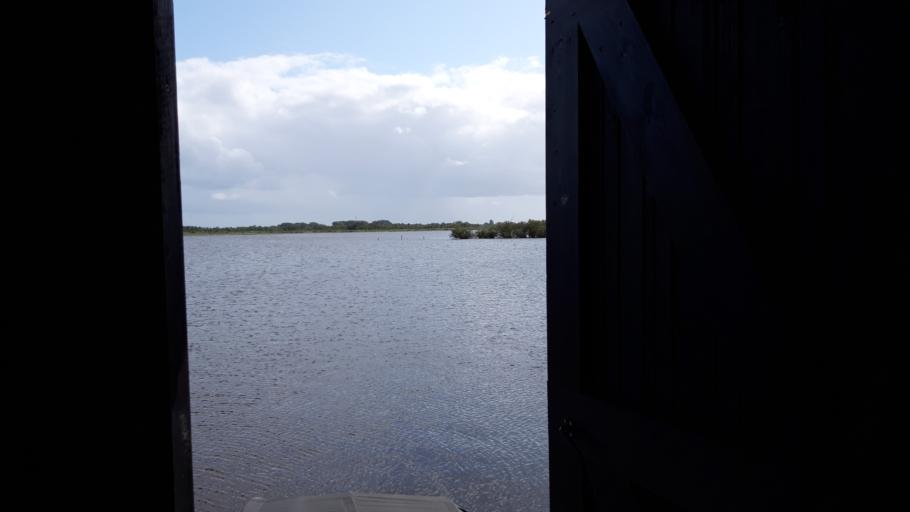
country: NL
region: Friesland
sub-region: Gemeente Boarnsterhim
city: Warten
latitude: 53.1165
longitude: 5.9273
